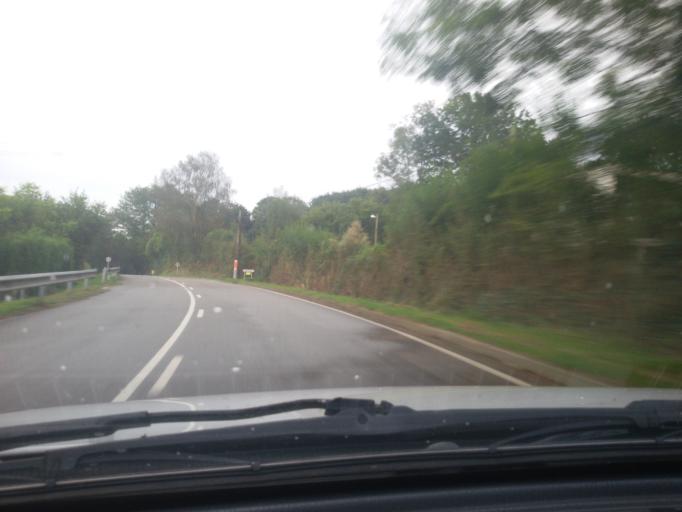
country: ES
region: Asturias
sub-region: Province of Asturias
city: Norena
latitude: 43.3738
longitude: -5.7190
